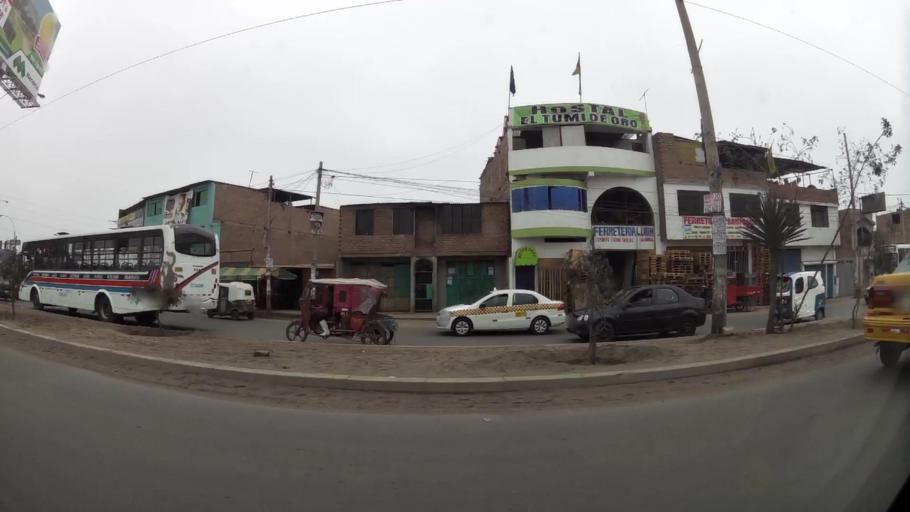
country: PE
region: Lima
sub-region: Lima
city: Punta Hermosa
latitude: -12.2400
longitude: -76.9129
